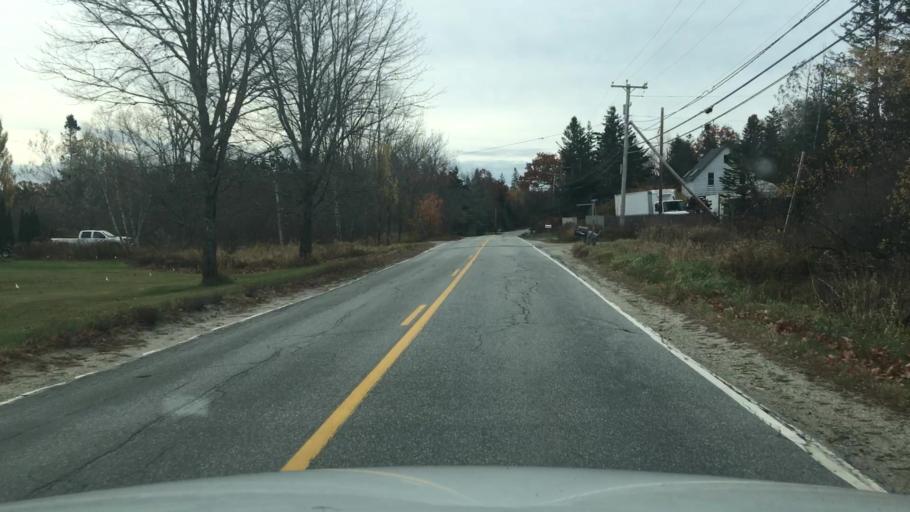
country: US
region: Maine
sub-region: Hancock County
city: Sedgwick
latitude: 44.3591
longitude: -68.5496
